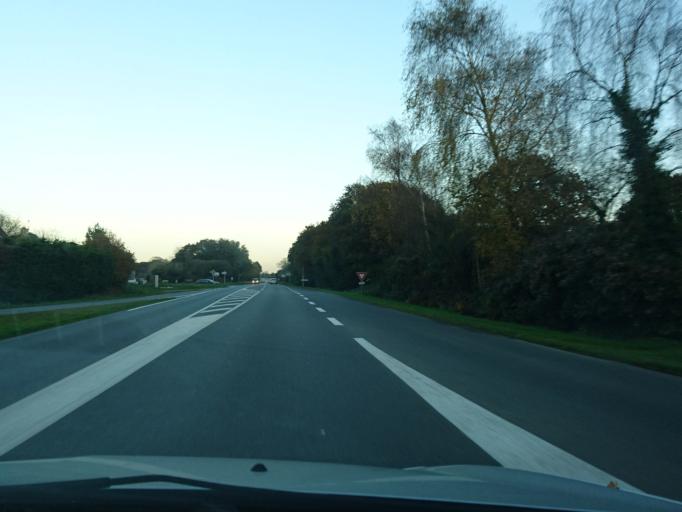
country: FR
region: Brittany
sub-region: Departement du Finistere
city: Saint-Renan
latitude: 48.4335
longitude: -4.6158
